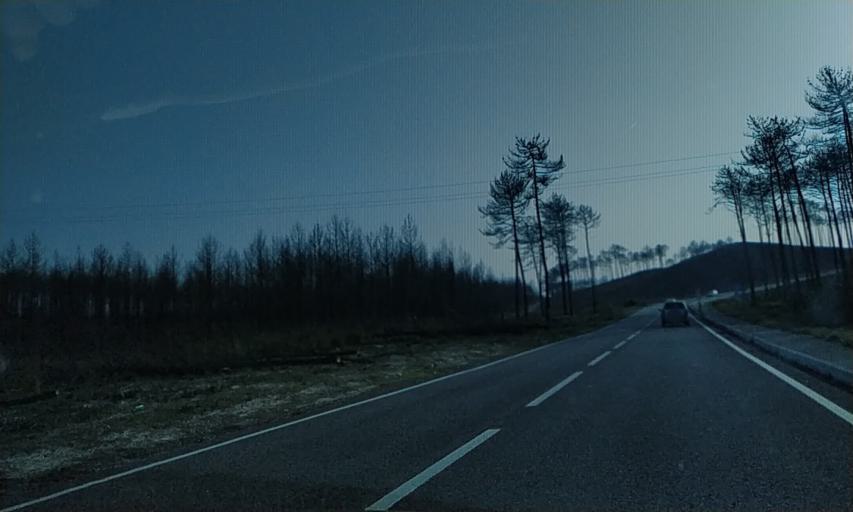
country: PT
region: Leiria
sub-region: Marinha Grande
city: Marinha Grande
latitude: 39.7461
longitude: -8.9788
